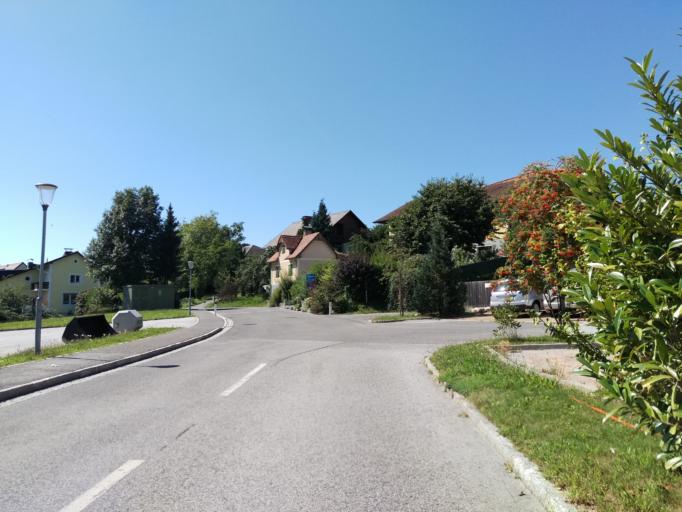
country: AT
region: Styria
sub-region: Politischer Bezirk Graz-Umgebung
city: Eggersdorf bei Graz
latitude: 47.0932
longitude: 15.5623
